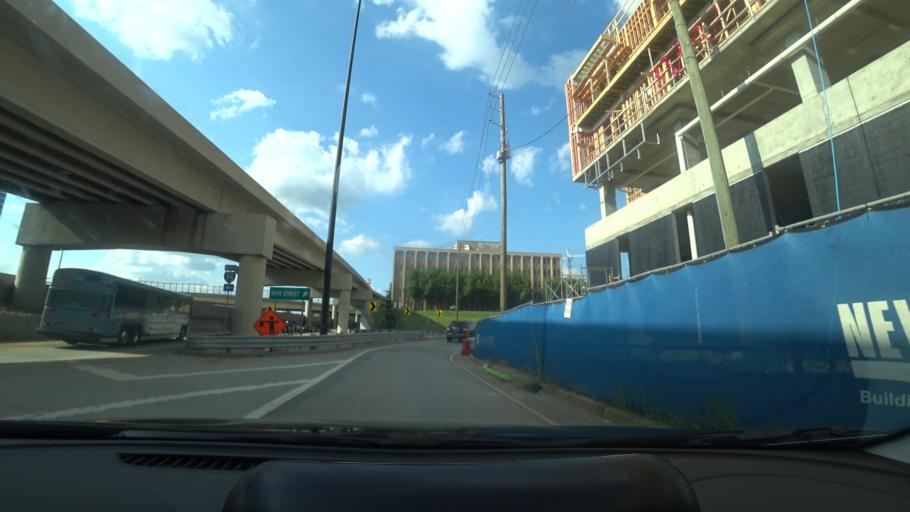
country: US
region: Georgia
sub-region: Fulton County
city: Atlanta
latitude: 33.7891
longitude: -84.3894
